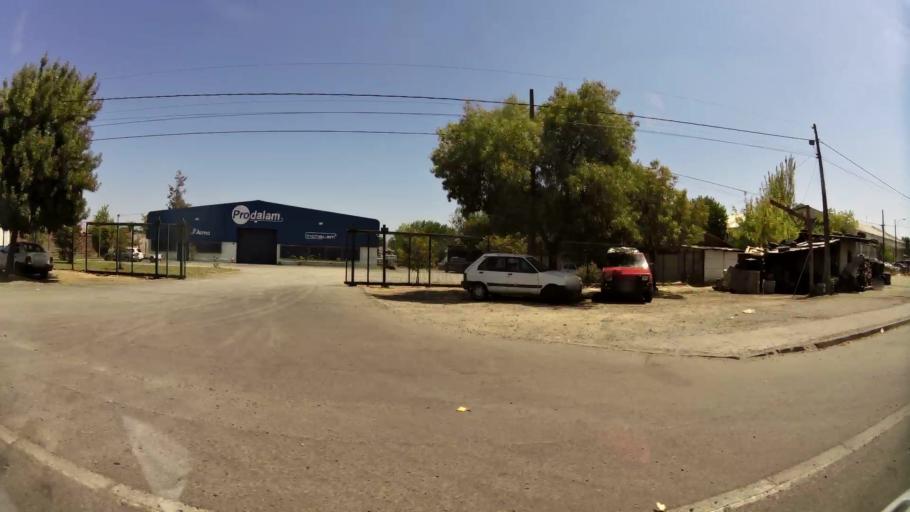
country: CL
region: Maule
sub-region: Provincia de Talca
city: Talca
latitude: -35.4338
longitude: -71.6381
